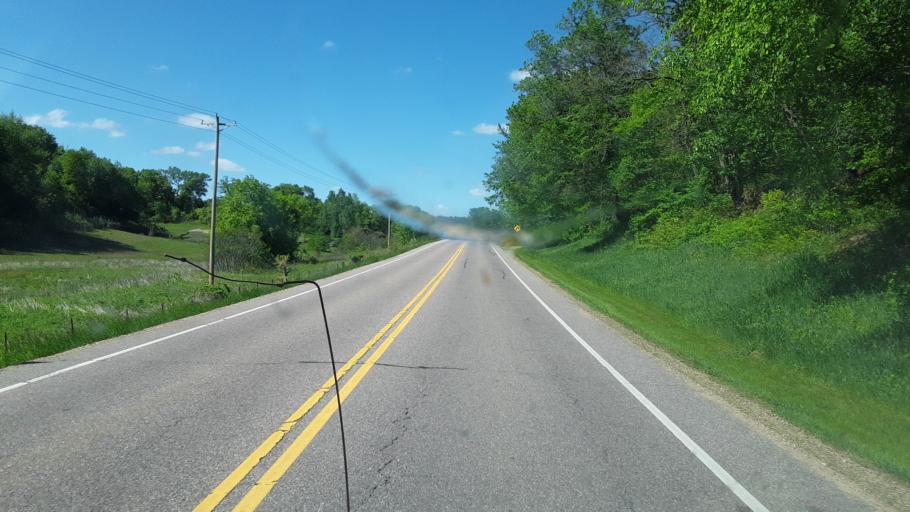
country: US
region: Wisconsin
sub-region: Sauk County
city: Reedsburg
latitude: 43.5973
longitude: -90.1260
